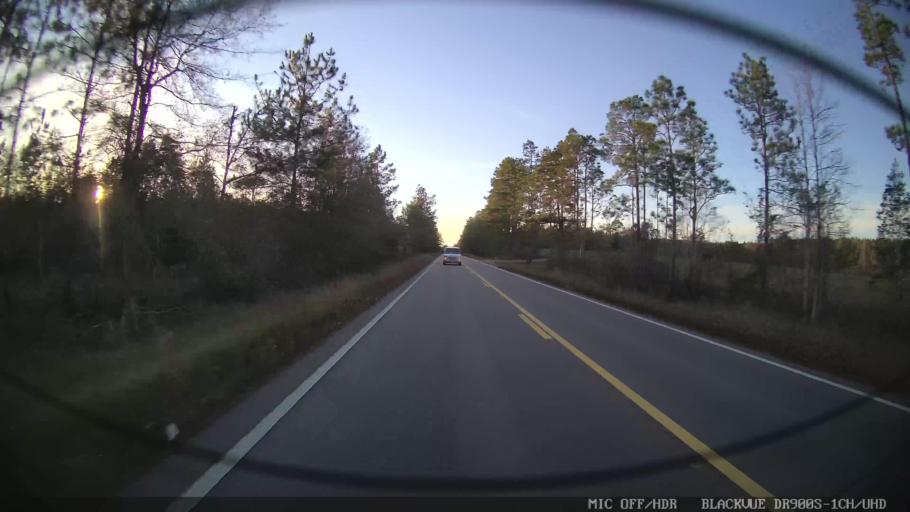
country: US
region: Mississippi
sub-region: Lamar County
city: Lumberton
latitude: 30.9986
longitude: -89.3010
